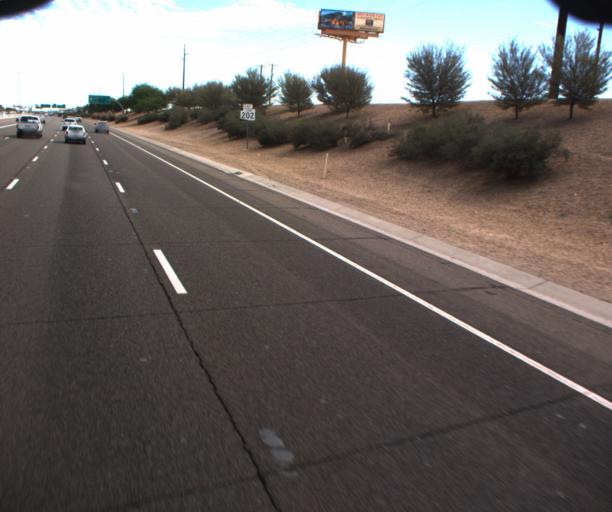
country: US
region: Arizona
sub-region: Maricopa County
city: Guadalupe
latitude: 33.2913
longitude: -111.9371
